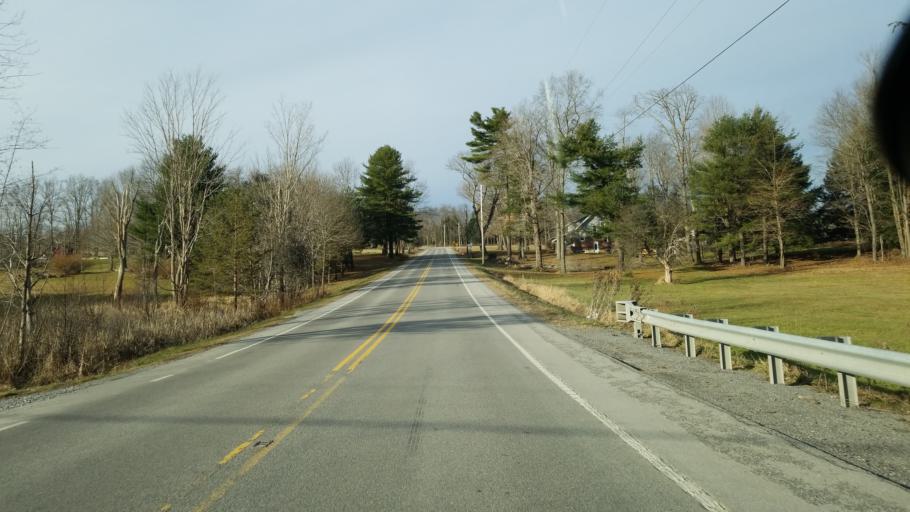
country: US
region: Pennsylvania
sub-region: Clearfield County
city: Curwensville
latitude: 41.0073
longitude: -78.6379
